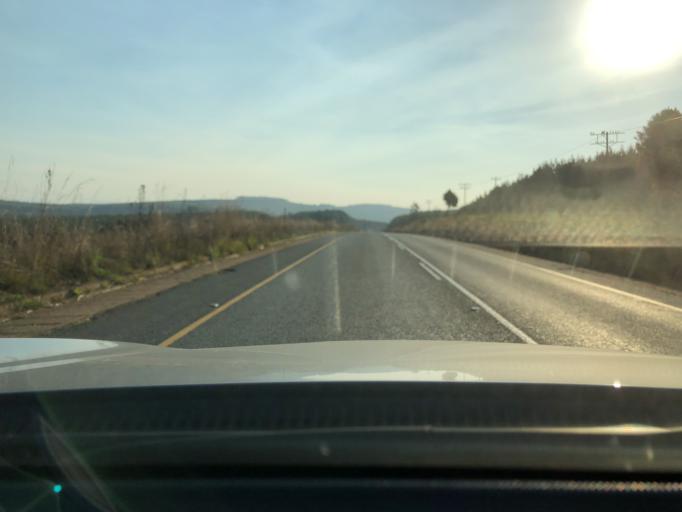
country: ZA
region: KwaZulu-Natal
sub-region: Sisonke District Municipality
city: Ixopo
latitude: -30.2005
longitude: 30.1086
